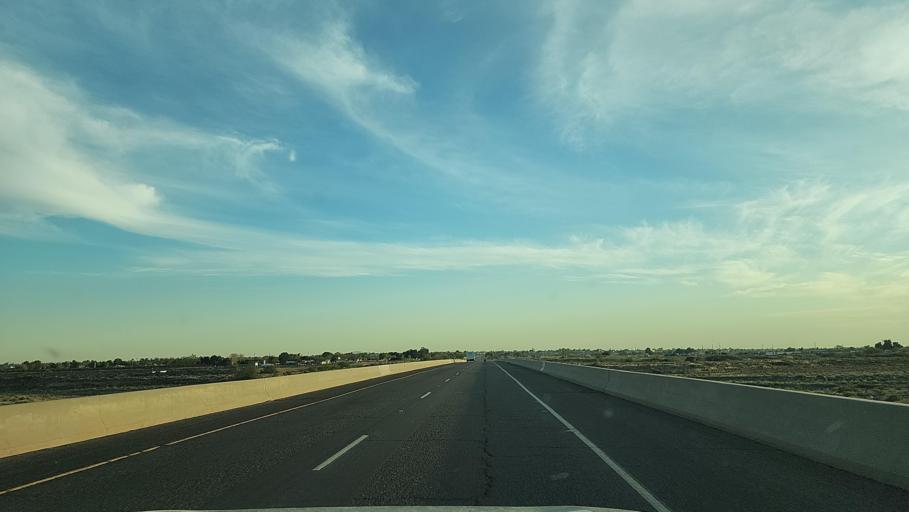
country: US
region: Arizona
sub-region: Maricopa County
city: Mesa
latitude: 33.4875
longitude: -111.7876
